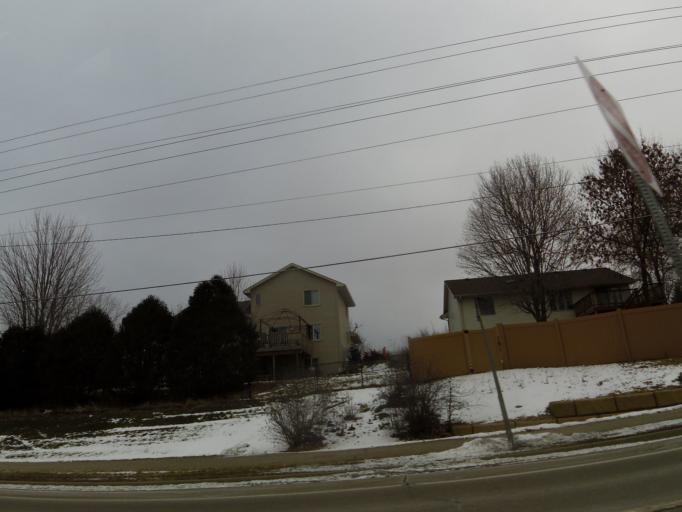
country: US
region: Minnesota
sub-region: Carver County
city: Waconia
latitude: 44.8356
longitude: -93.7885
